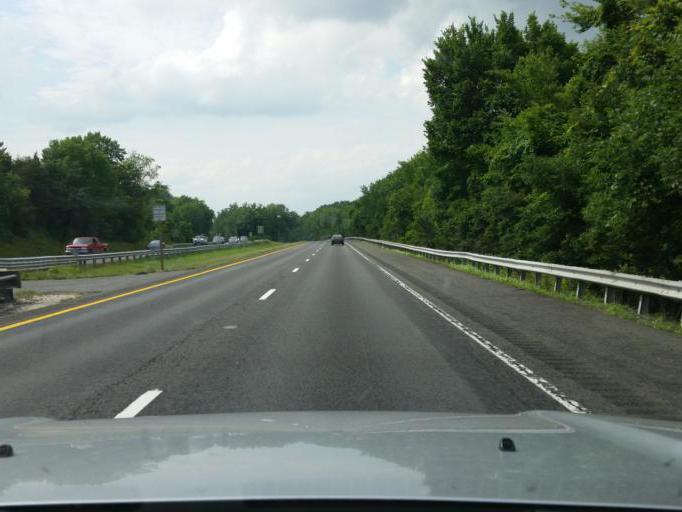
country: US
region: Maryland
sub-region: Montgomery County
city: Clarksburg
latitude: 39.2519
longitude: -77.3015
